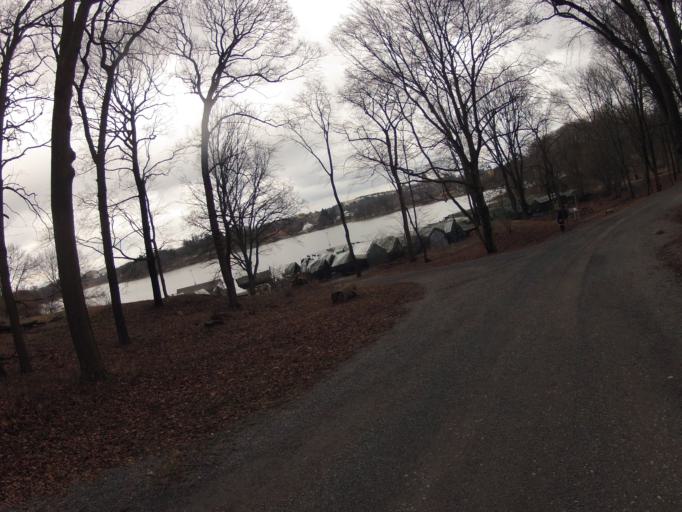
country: SE
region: Stockholm
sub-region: Norrtalje Kommun
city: Bergshamra
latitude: 59.3664
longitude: 18.0352
